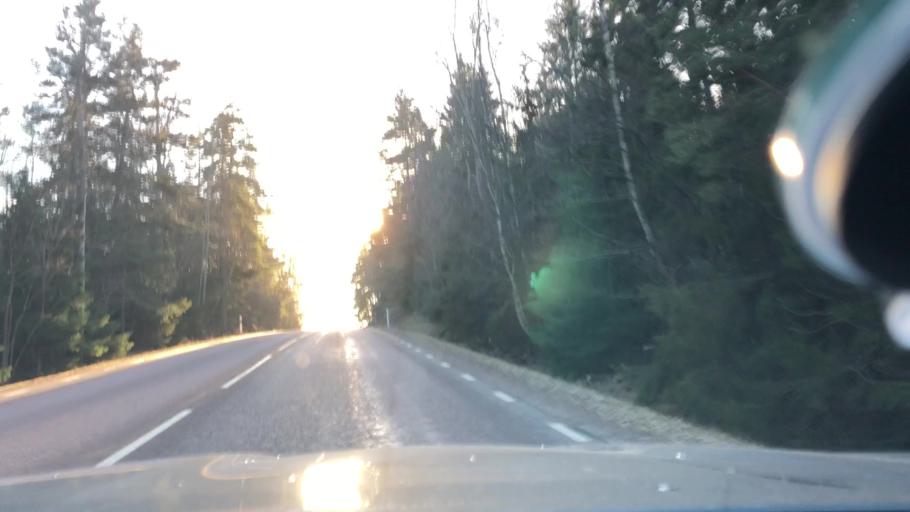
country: SE
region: Stockholm
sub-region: Sodertalje Kommun
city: Pershagen
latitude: 59.0434
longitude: 17.6044
